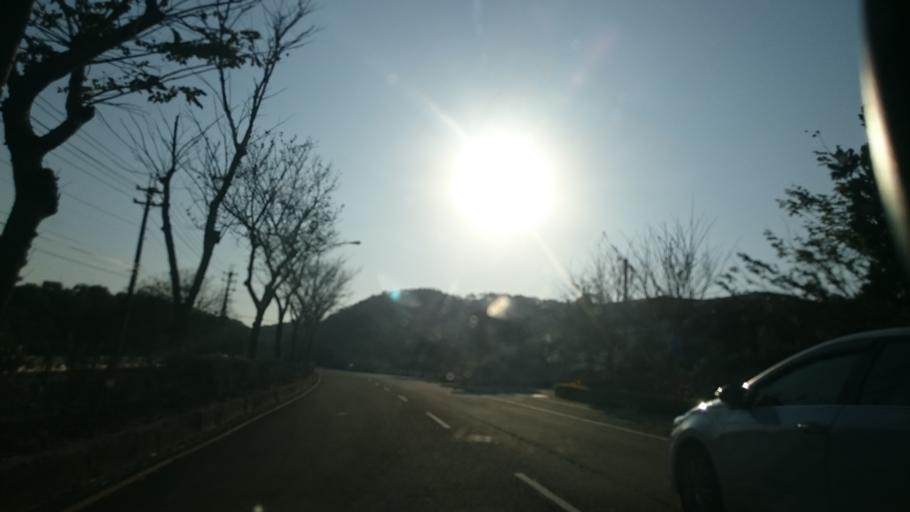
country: TW
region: Taiwan
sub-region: Miaoli
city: Miaoli
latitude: 24.6499
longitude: 120.8475
